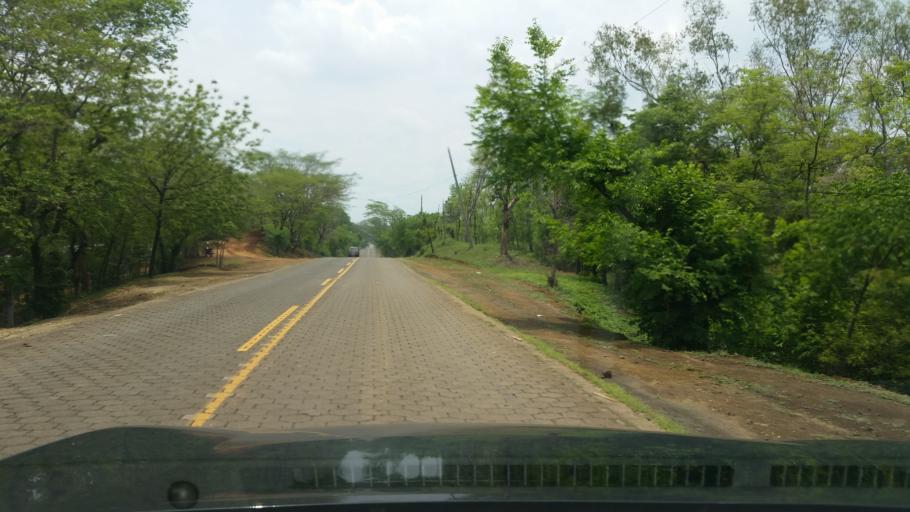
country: NI
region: Managua
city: Carlos Fonseca Amador
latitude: 11.9492
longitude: -86.5096
